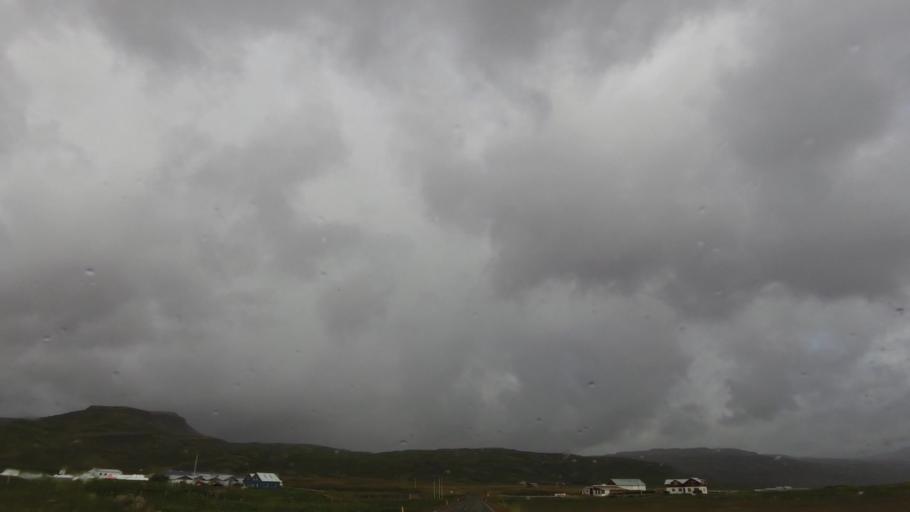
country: IS
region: Westfjords
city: Isafjoerdur
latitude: 65.5245
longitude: -23.1912
